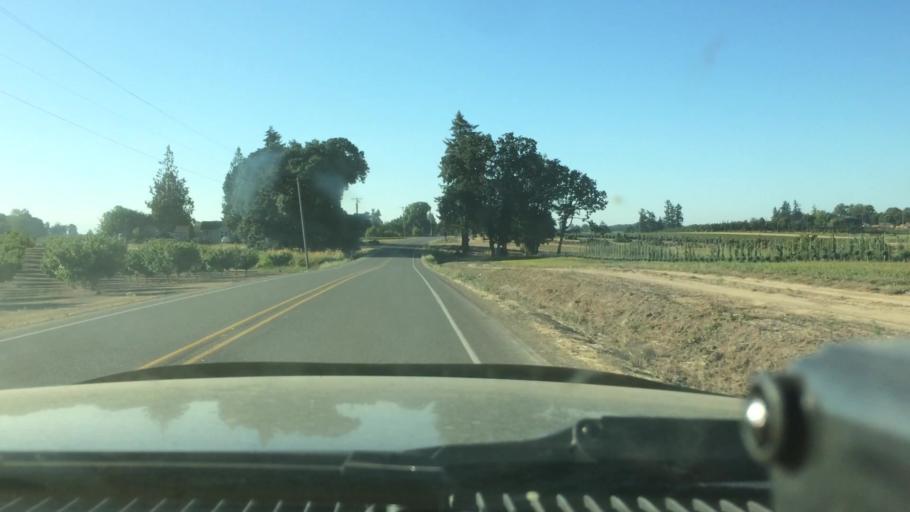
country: US
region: Oregon
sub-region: Marion County
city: Gervais
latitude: 45.1238
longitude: -122.9876
